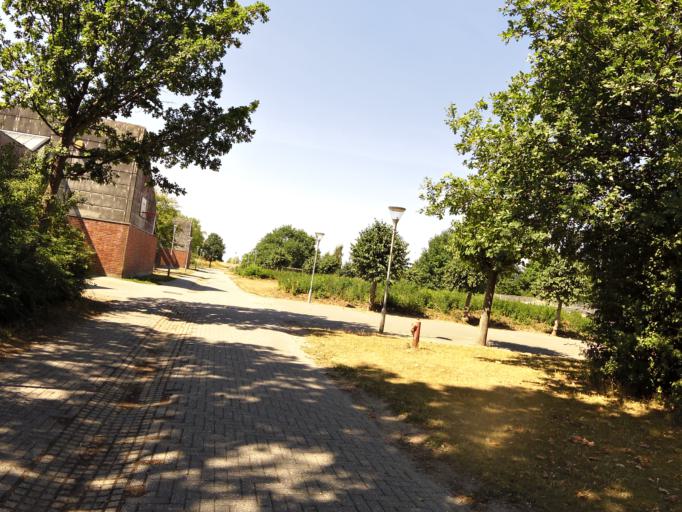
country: DK
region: Capital Region
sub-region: Fredensborg Kommune
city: Niva
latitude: 55.9410
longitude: 12.4915
